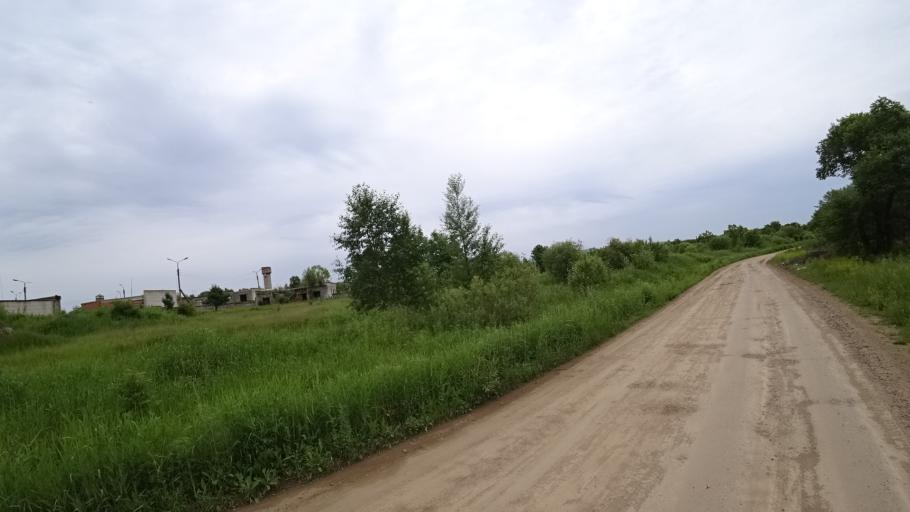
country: RU
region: Primorskiy
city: Arsen'yev
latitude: 44.1991
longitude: 133.3096
